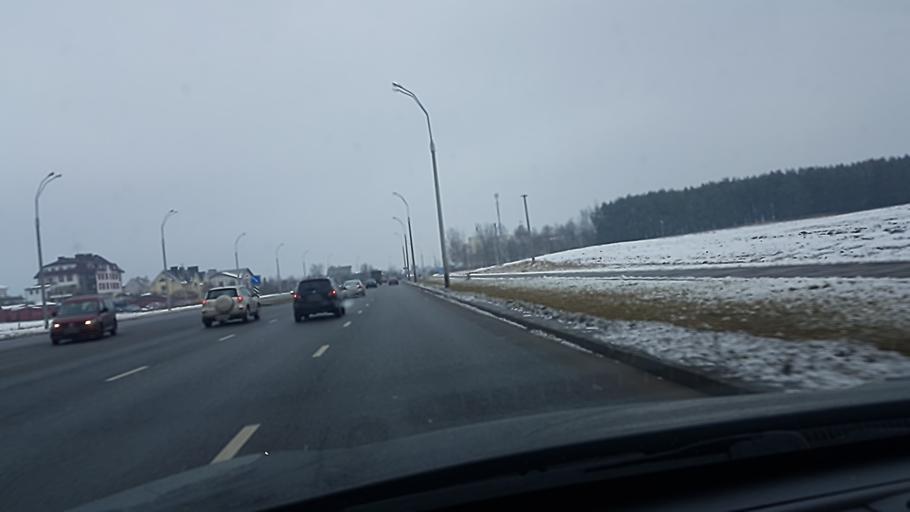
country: BY
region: Minsk
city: Minsk
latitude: 53.9500
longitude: 27.5359
